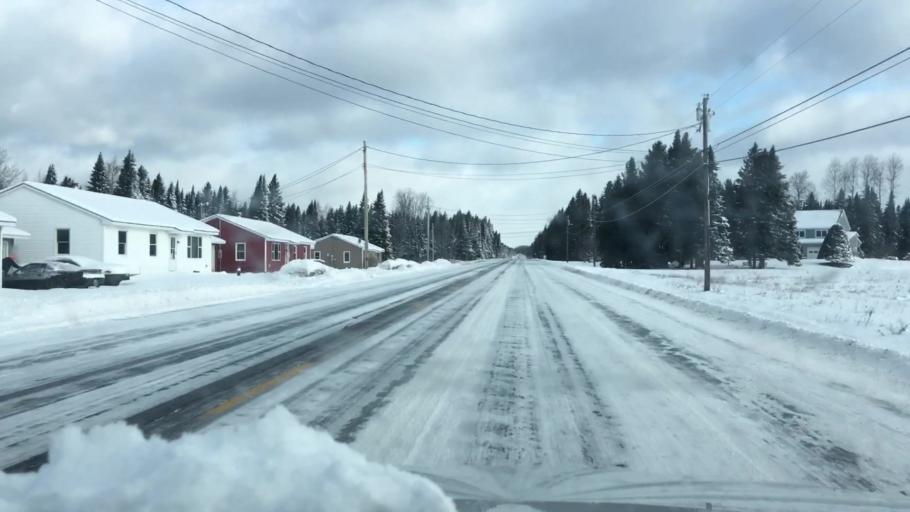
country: US
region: Maine
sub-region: Aroostook County
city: Madawaska
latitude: 47.0118
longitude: -68.0190
